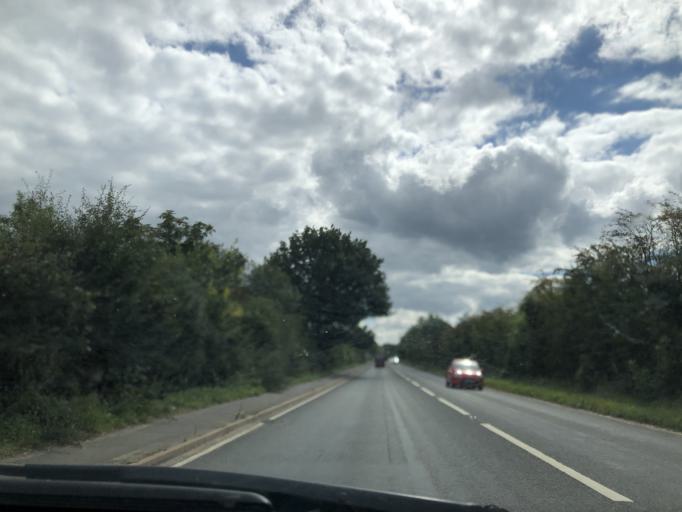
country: GB
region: England
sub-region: Kent
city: Halstead
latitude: 51.3266
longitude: 0.1534
